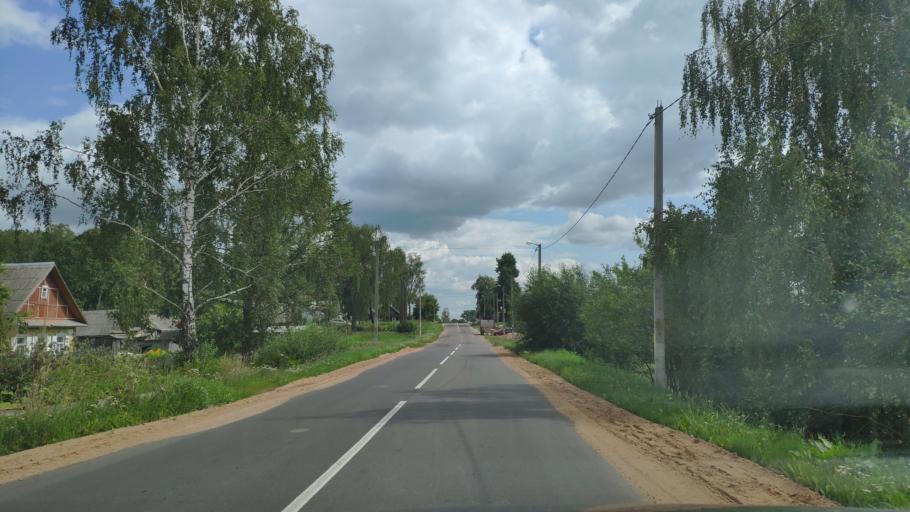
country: BY
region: Minsk
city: Khatsyezhyna
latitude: 53.8886
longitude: 27.2642
